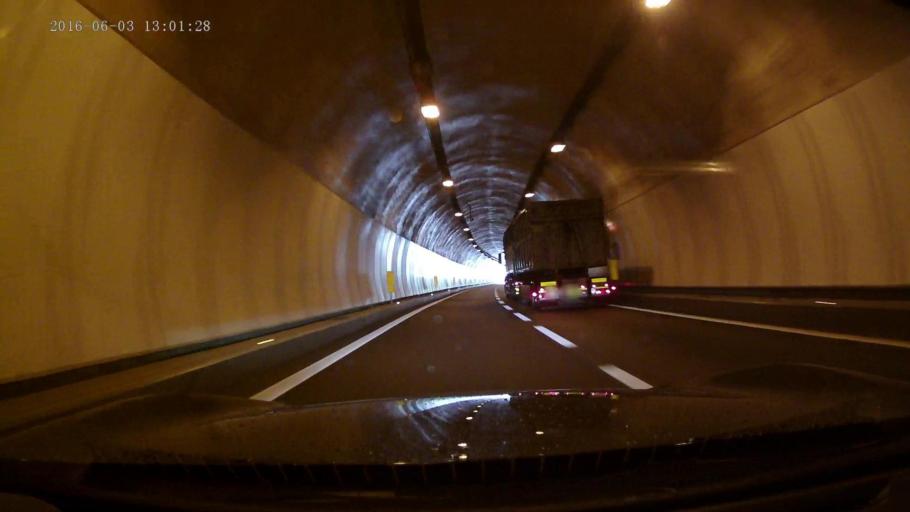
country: IT
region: Trentino-Alto Adige
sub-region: Bolzano
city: Fortezza
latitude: 46.7869
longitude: 11.6151
